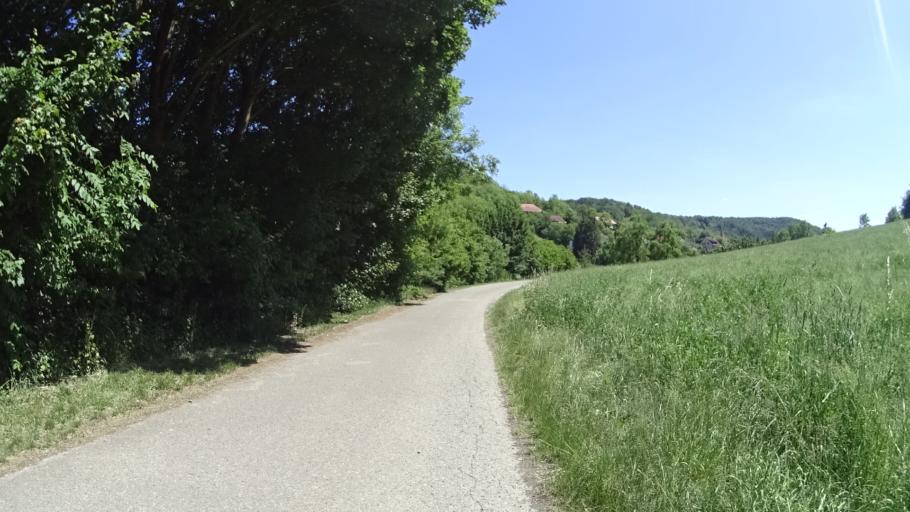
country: DE
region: Bavaria
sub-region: Regierungsbezirk Mittelfranken
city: Adelshofen
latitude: 49.4204
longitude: 10.1487
